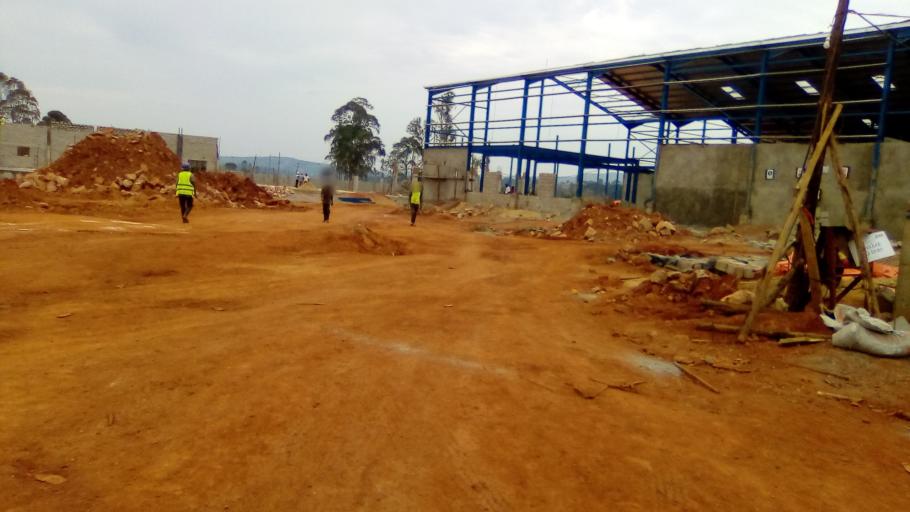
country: UG
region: Central Region
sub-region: Wakiso District
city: Kajansi
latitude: 0.1663
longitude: 32.5115
